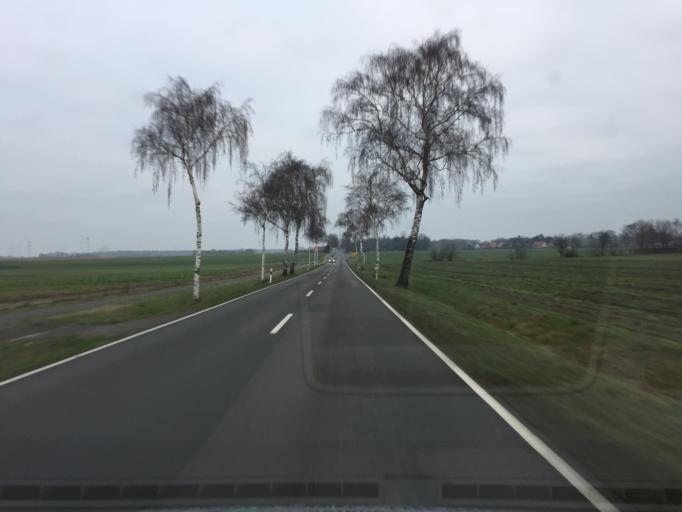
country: DE
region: Lower Saxony
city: Sulingen
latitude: 52.6986
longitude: 8.8057
